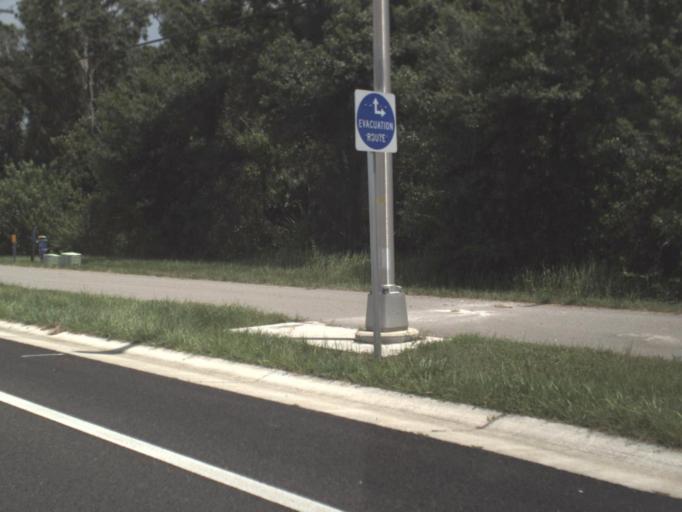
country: US
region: Florida
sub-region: Hillsborough County
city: Sun City Center
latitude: 27.7685
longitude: -82.3349
